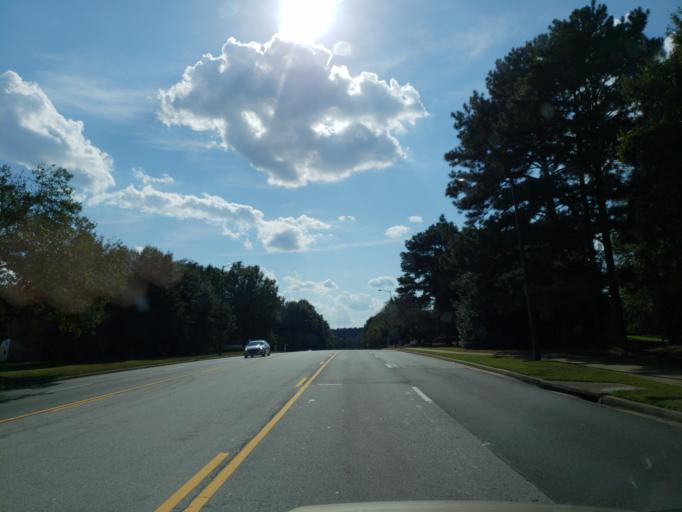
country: US
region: Georgia
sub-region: Cobb County
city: Mableton
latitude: 33.7639
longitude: -84.5607
